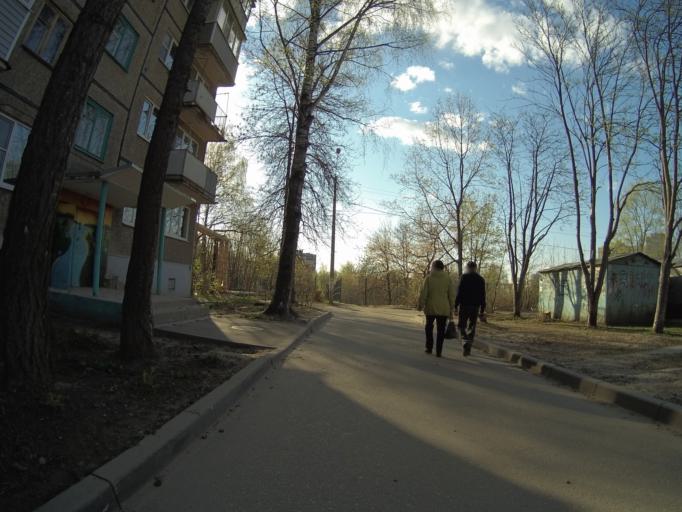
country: RU
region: Vladimir
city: Vladimir
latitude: 56.1339
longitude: 40.3574
